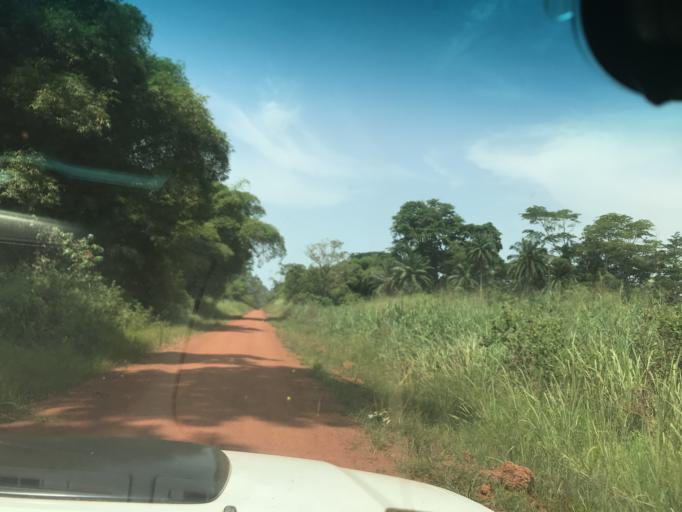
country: CD
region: Eastern Province
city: Aketi
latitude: 2.8746
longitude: 23.9551
